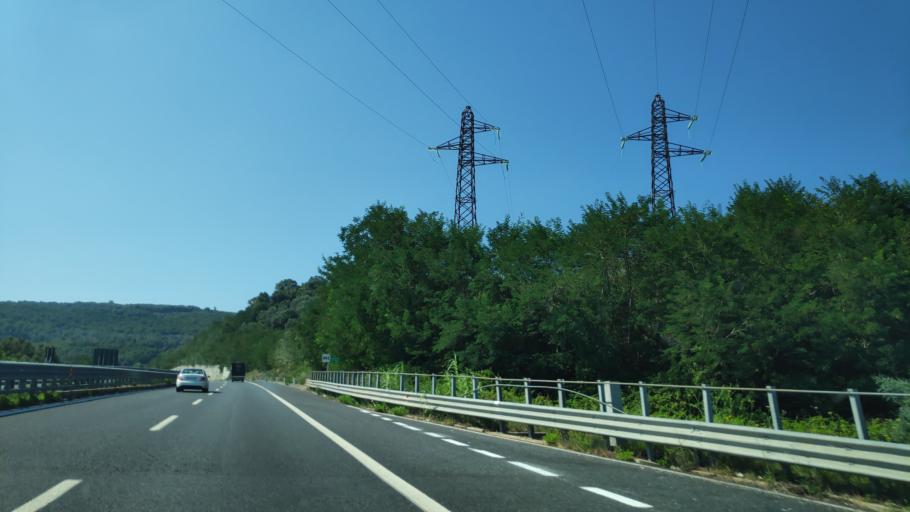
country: IT
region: Calabria
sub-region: Provincia di Reggio Calabria
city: Seminara
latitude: 38.3623
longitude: 15.8650
